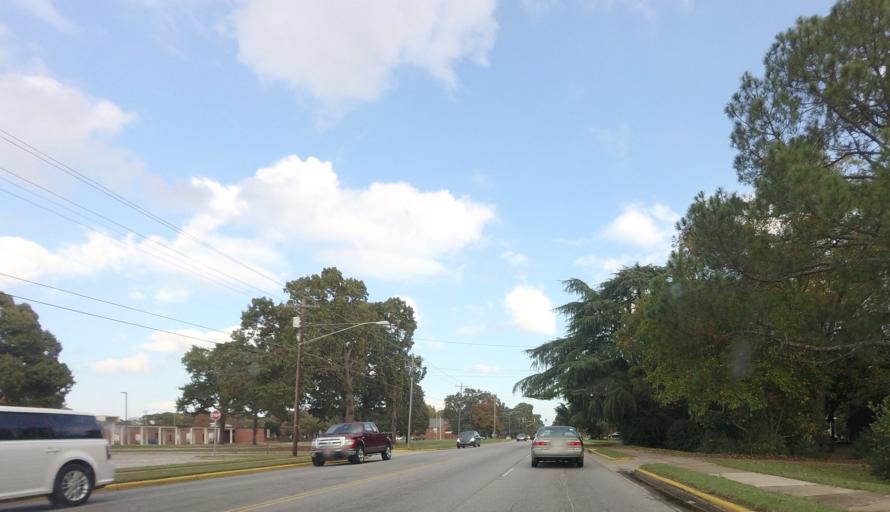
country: US
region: Georgia
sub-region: Houston County
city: Warner Robins
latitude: 32.6263
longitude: -83.6309
